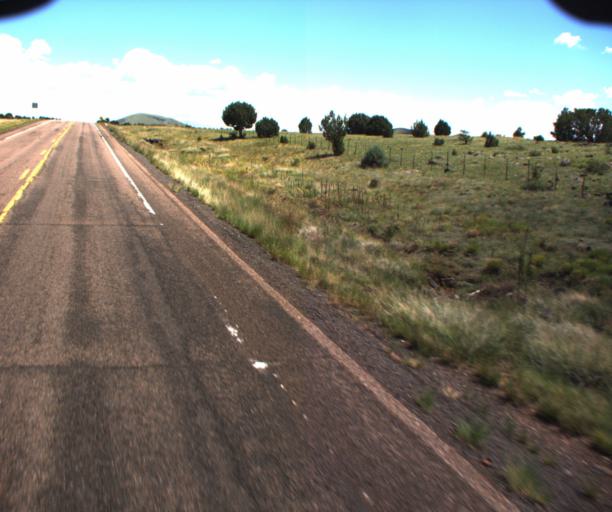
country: US
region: Arizona
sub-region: Apache County
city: Springerville
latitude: 34.2570
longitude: -109.5487
